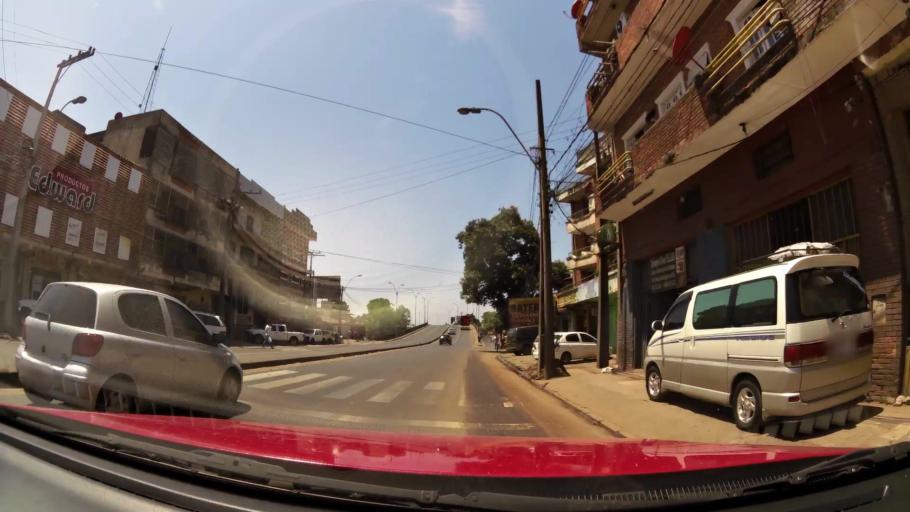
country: PY
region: Central
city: Fernando de la Mora
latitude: -25.3214
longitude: -57.5618
